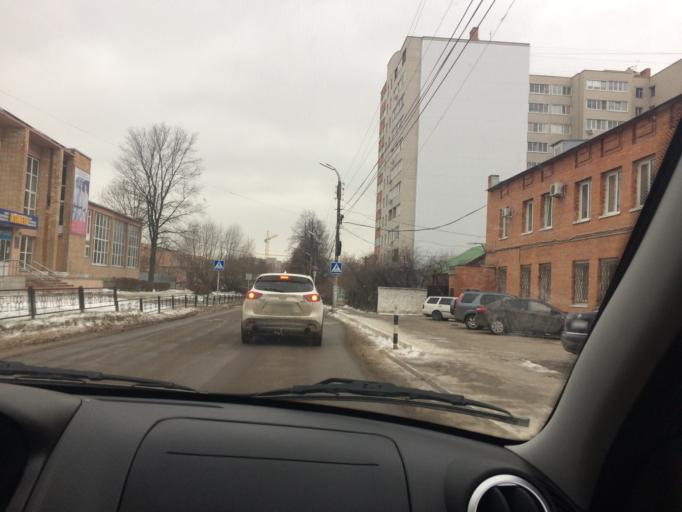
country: RU
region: Rjazan
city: Ryazan'
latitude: 54.6181
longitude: 39.7144
